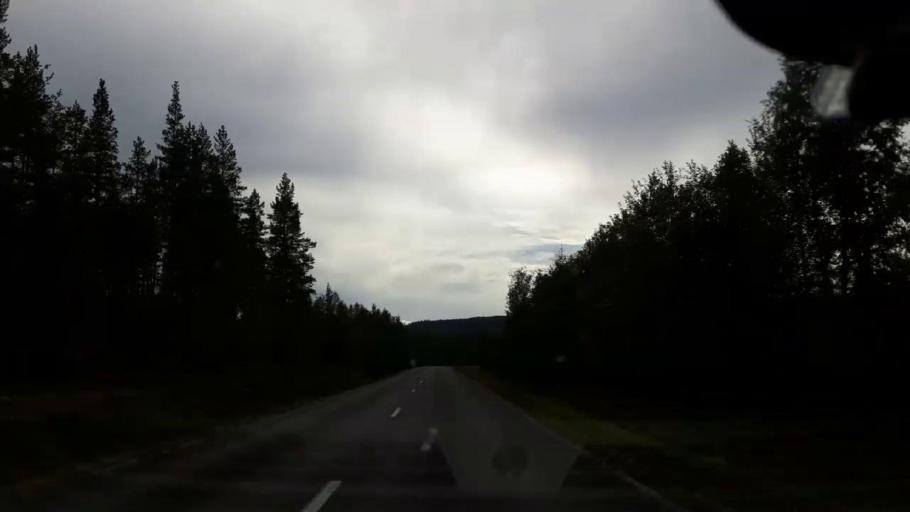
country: SE
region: Jaemtland
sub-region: Ragunda Kommun
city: Hammarstrand
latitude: 63.0468
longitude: 15.9279
